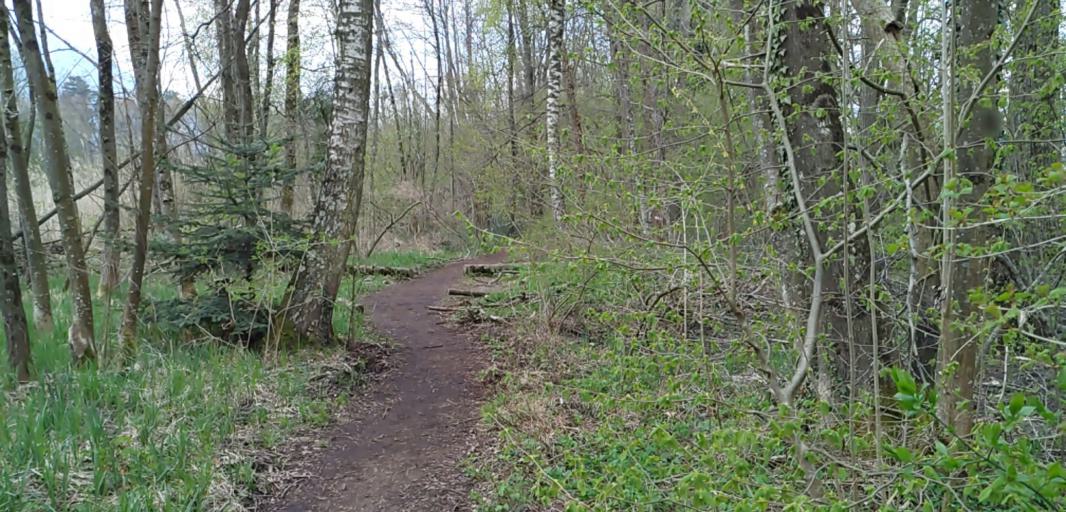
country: CH
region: Vaud
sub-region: Aigle District
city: Villeneuve
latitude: 46.3958
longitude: 6.9058
